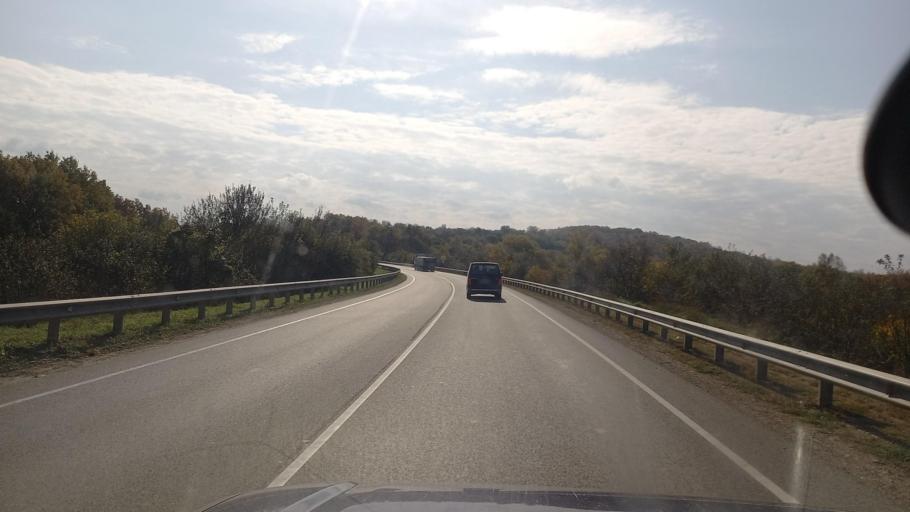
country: RU
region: Krasnodarskiy
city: Abinsk
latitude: 44.8523
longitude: 38.1345
